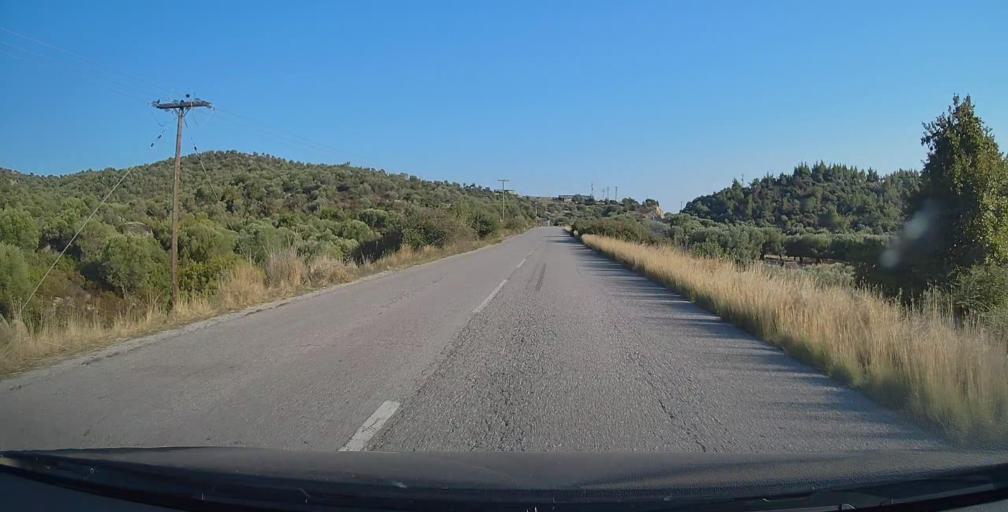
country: GR
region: Central Macedonia
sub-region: Nomos Chalkidikis
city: Sykia
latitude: 40.0032
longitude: 23.8869
